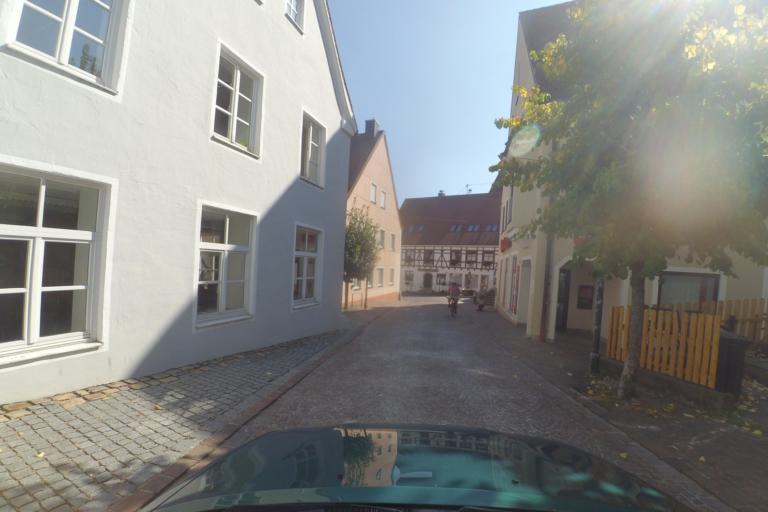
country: DE
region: Bavaria
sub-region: Swabia
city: Harburg
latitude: 48.7875
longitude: 10.6888
